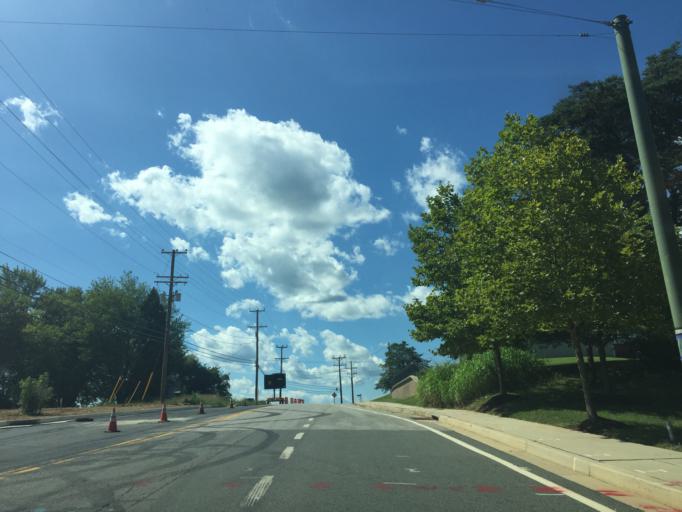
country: US
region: Maryland
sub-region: Baltimore County
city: White Marsh
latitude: 39.3871
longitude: -76.4370
